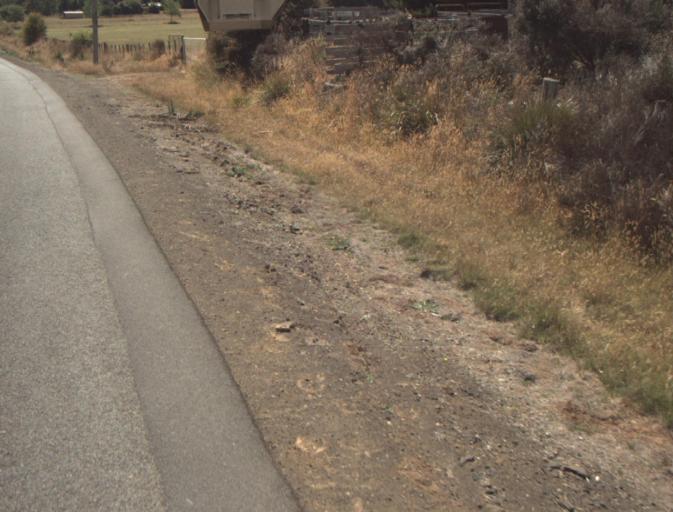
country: AU
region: Tasmania
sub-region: Launceston
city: Newstead
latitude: -41.3255
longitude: 147.3179
